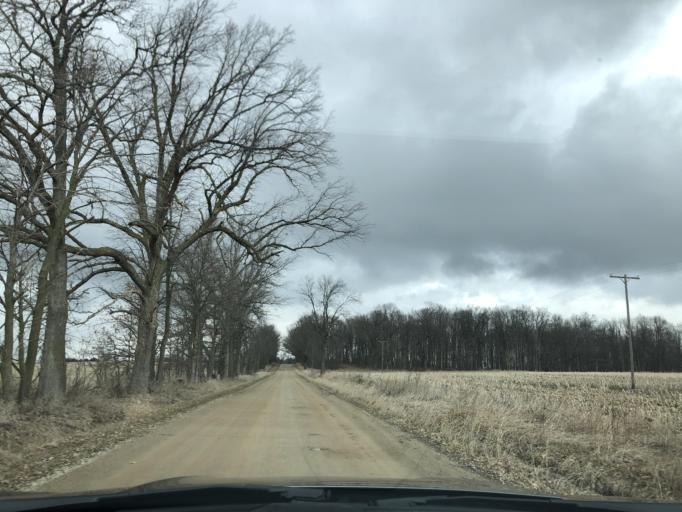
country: US
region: Michigan
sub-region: Clinton County
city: Saint Johns
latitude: 43.0985
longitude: -84.6106
